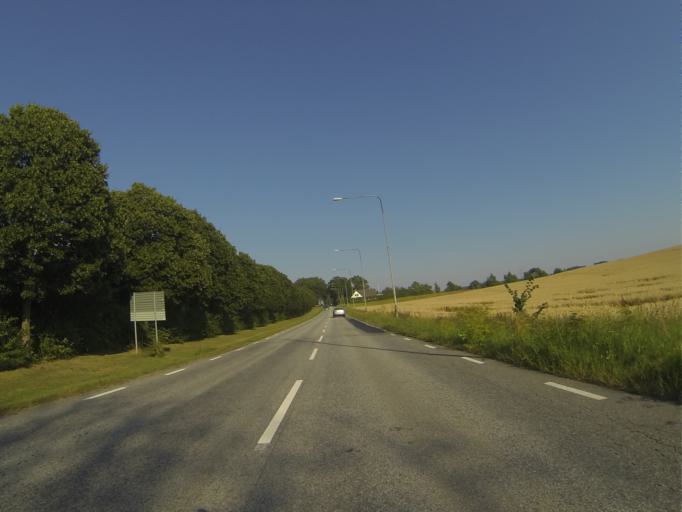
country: SE
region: Skane
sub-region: Svedala Kommun
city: Klagerup
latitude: 55.5767
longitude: 13.1806
